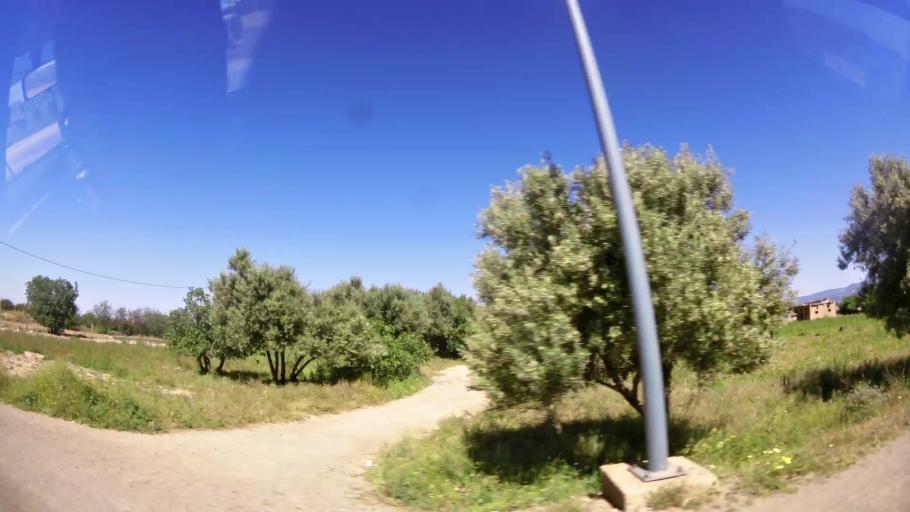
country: MA
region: Oriental
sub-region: Oujda-Angad
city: Oujda
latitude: 34.7010
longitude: -1.8566
